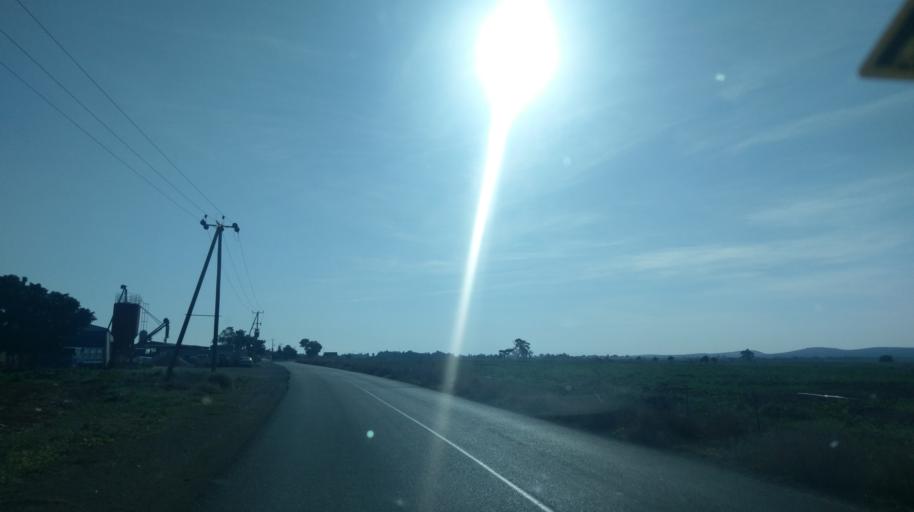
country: CY
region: Larnaka
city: Pergamos
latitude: 35.0622
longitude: 33.7134
